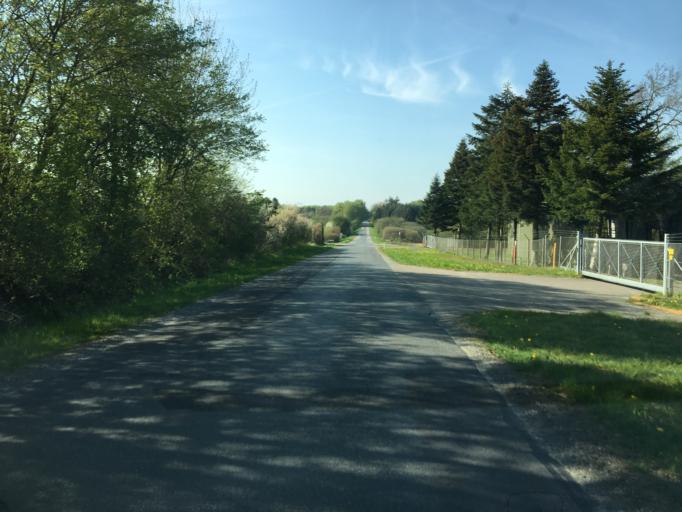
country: DK
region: South Denmark
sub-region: Haderslev Kommune
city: Vojens
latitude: 55.2362
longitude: 9.3270
